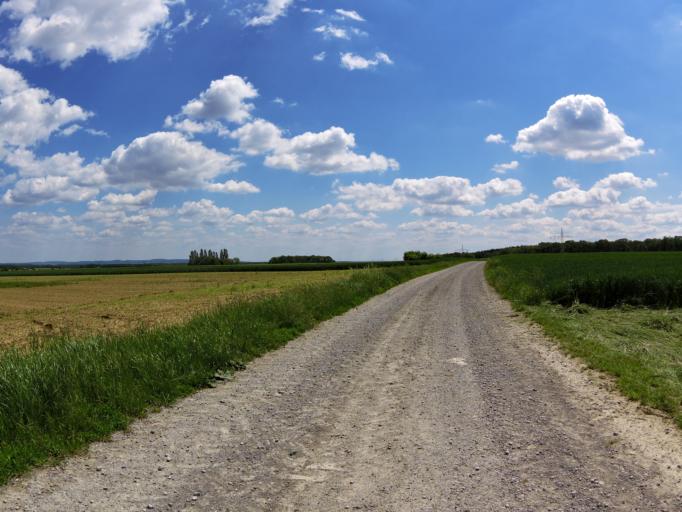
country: DE
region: Bavaria
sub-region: Regierungsbezirk Unterfranken
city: Theilheim
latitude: 49.7386
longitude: 10.0640
